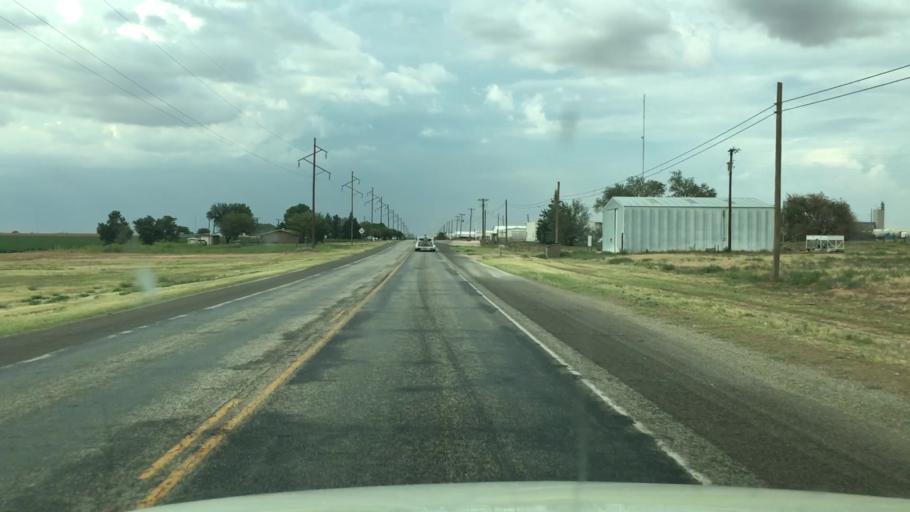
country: US
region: Texas
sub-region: Terry County
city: Brownfield
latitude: 33.1678
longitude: -102.2915
